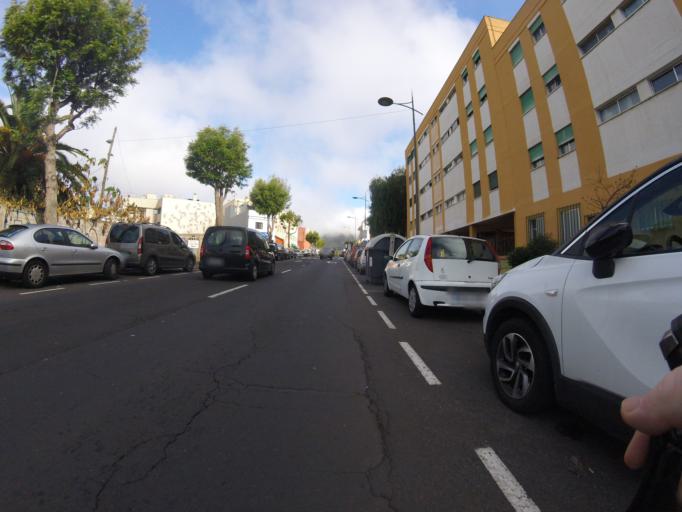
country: ES
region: Canary Islands
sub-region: Provincia de Santa Cruz de Tenerife
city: La Laguna
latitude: 28.4883
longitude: -16.3259
